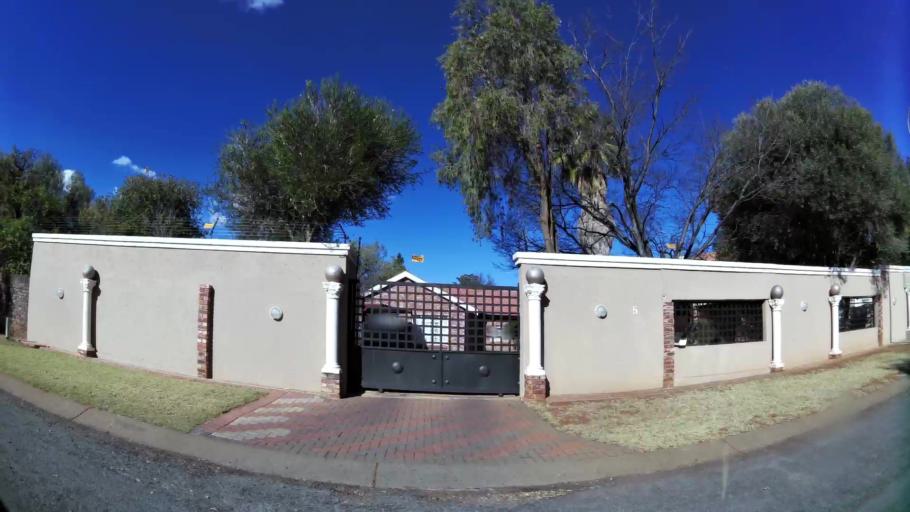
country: ZA
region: Gauteng
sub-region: West Rand District Municipality
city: Carletonville
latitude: -26.3646
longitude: 27.3696
